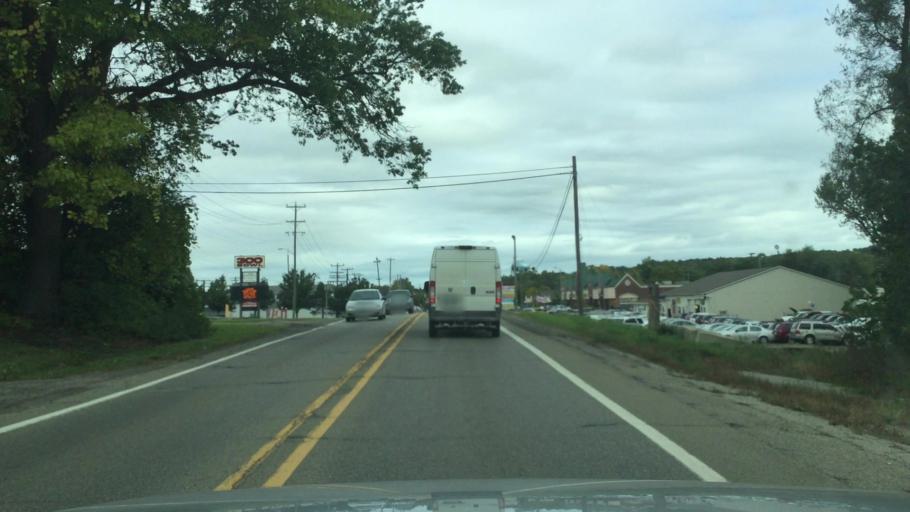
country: US
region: Michigan
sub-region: Oakland County
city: Keego Harbor
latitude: 42.6366
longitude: -83.3554
